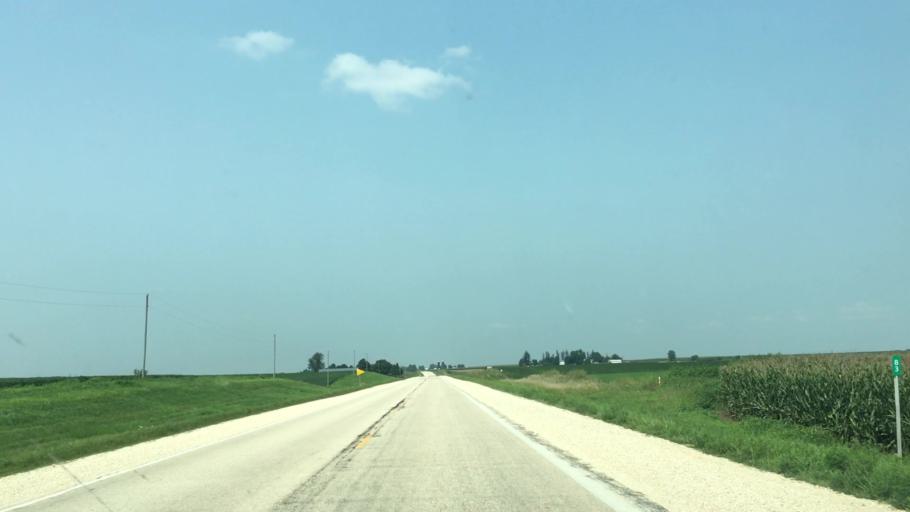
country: US
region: Iowa
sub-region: Fayette County
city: West Union
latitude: 42.9856
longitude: -91.8242
